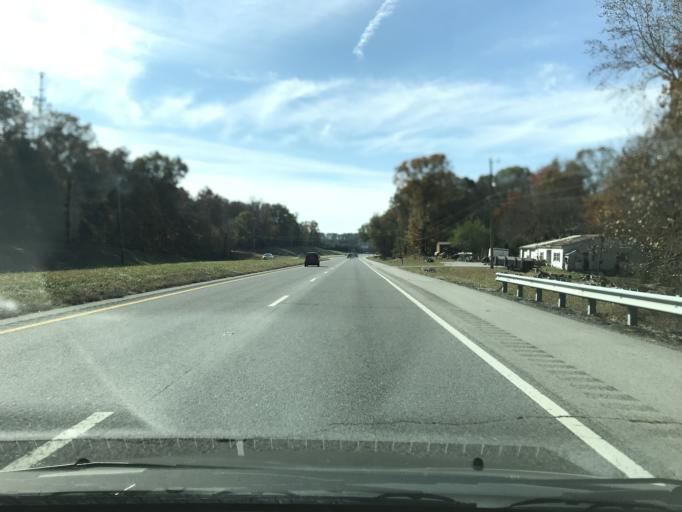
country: US
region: Tennessee
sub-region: Coffee County
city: Manchester
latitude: 35.4182
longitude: -86.1146
